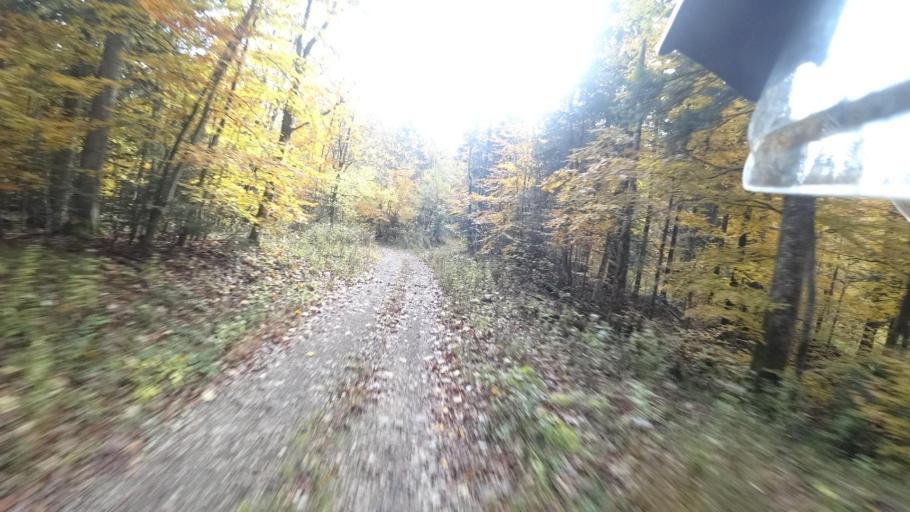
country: HR
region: Karlovacka
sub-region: Grad Ogulin
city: Ogulin
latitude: 45.2106
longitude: 15.0812
